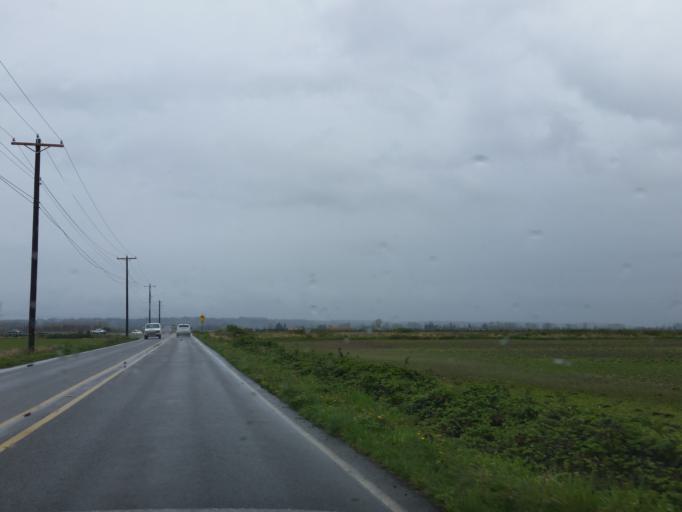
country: US
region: Washington
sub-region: Snohomish County
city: Silver Firs
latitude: 47.8953
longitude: -122.1414
